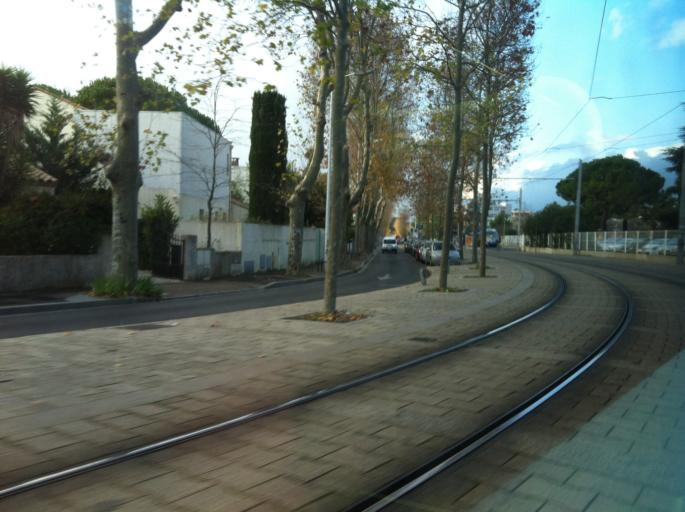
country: FR
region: Languedoc-Roussillon
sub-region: Departement de l'Herault
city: Montpellier
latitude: 43.6296
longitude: 3.8632
